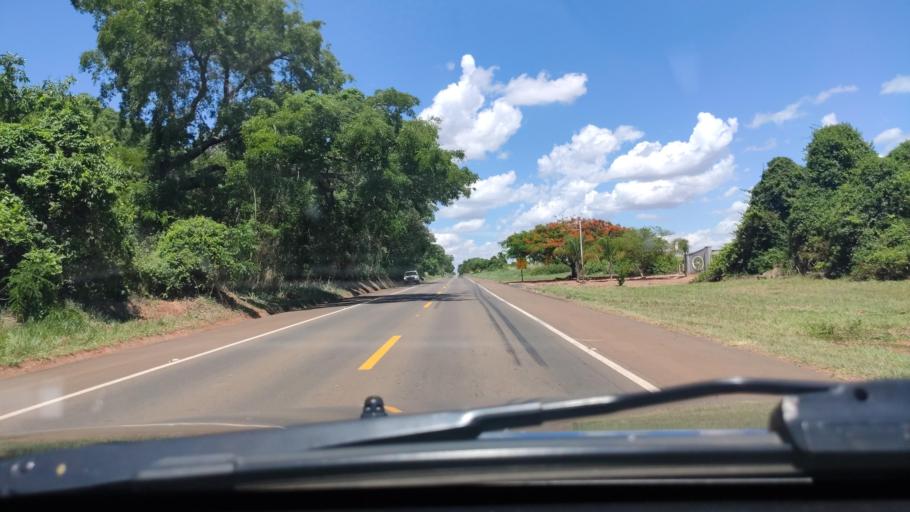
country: BR
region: Sao Paulo
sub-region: Boa Esperanca Do Sul
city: Boa Esperanca do Sul
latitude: -22.0693
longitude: -48.3885
